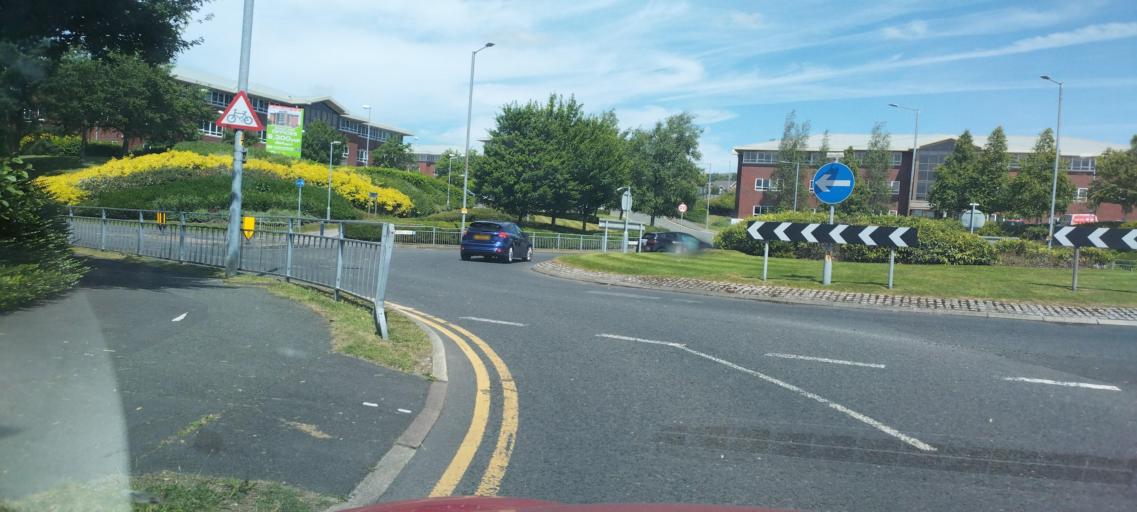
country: GB
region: England
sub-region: Borough of Bolton
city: Horwich
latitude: 53.5868
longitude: -2.5384
